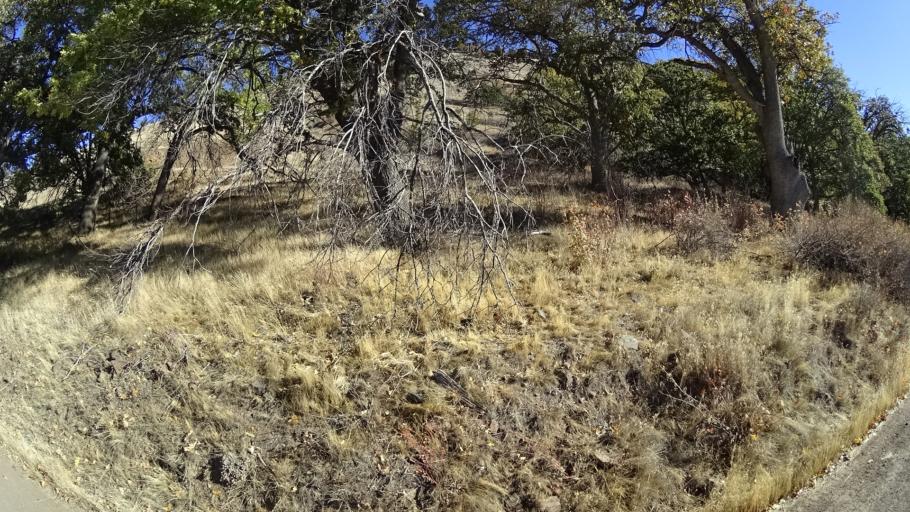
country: US
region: California
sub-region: Siskiyou County
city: Montague
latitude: 41.9868
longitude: -122.3074
